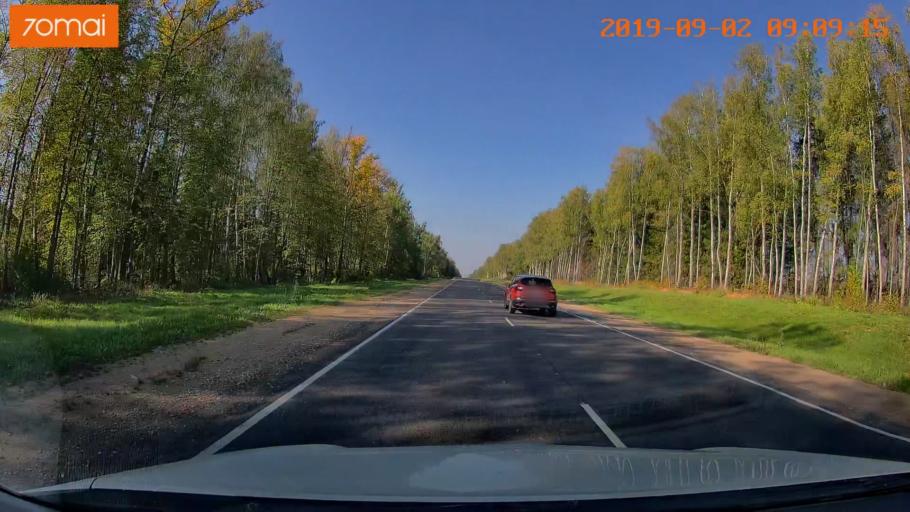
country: RU
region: Kaluga
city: Myatlevo
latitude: 54.8858
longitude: 35.6289
